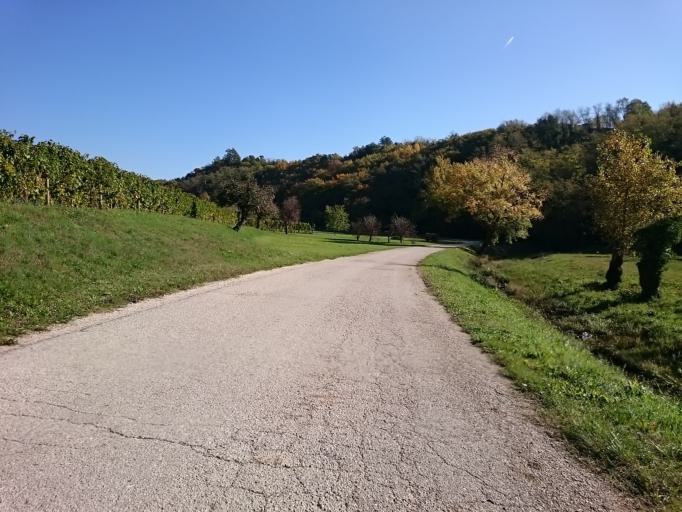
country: HR
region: Istarska
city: Buje
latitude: 45.4426
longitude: 13.7090
